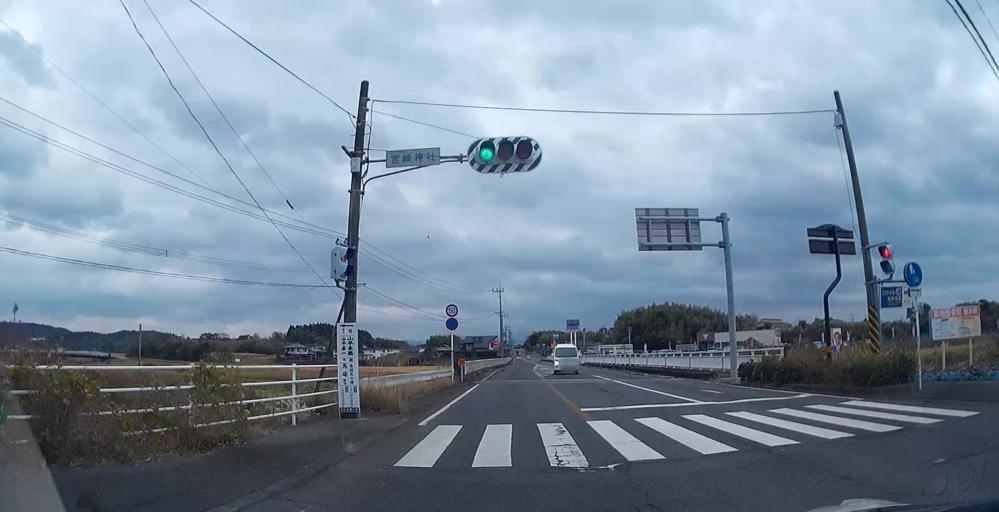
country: JP
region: Kagoshima
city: Akune
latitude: 32.0836
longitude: 130.1985
